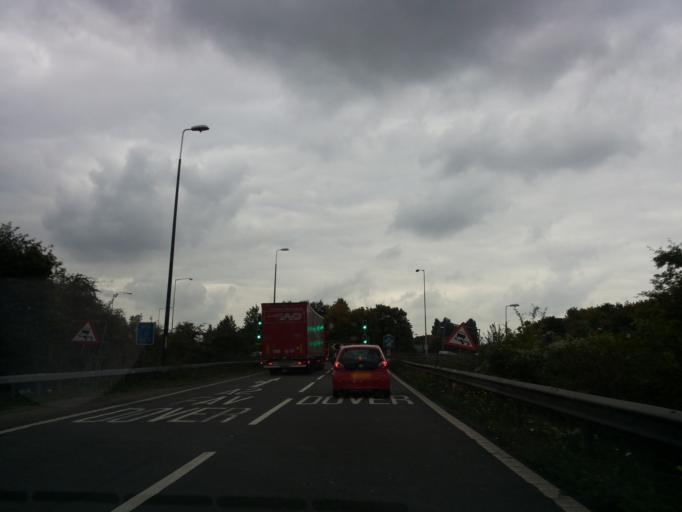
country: GB
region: England
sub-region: Kent
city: Faversham
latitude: 51.3007
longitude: 0.9240
